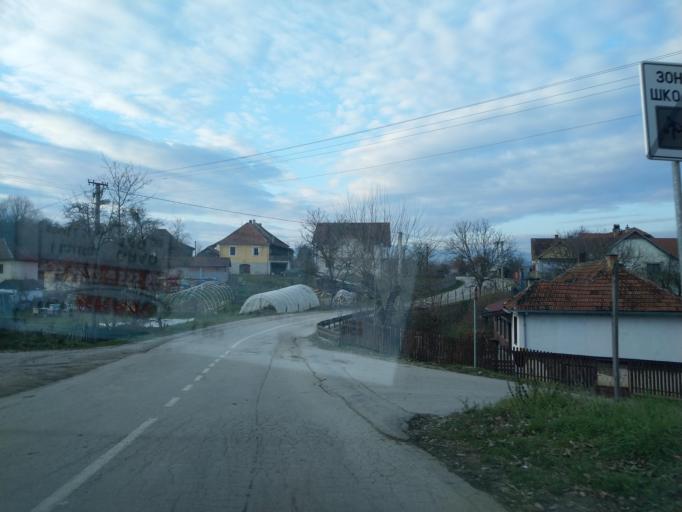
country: RS
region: Central Serbia
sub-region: Zlatiborski Okrug
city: Kosjeric
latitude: 43.9164
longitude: 19.9107
